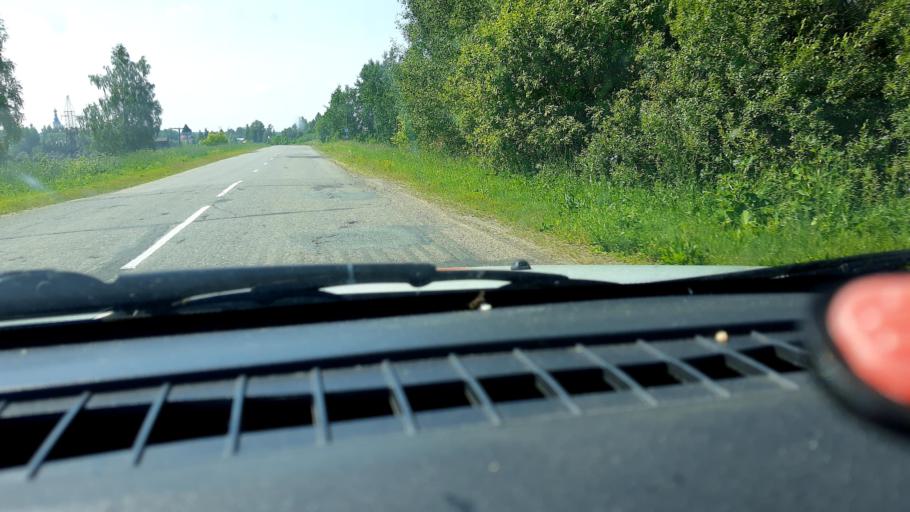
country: RU
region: Nizjnij Novgorod
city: Sharanga
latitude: 57.0580
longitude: 46.5463
